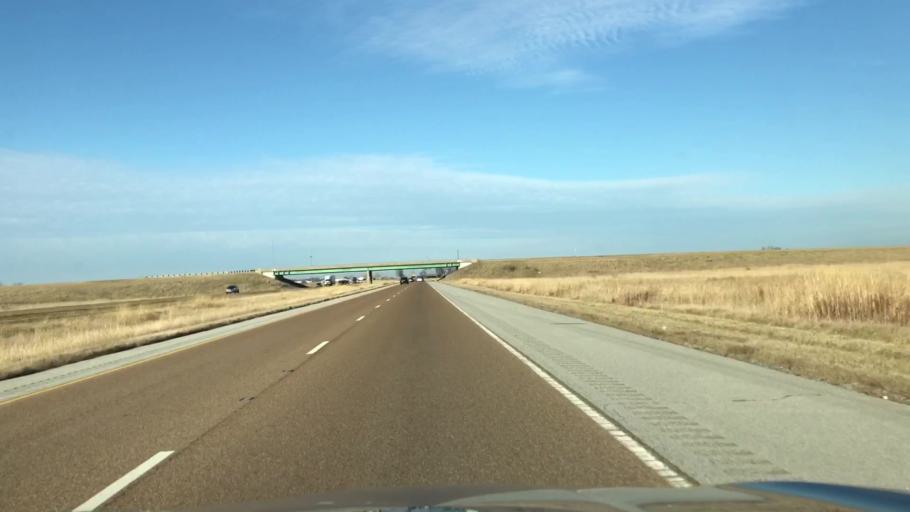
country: US
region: Illinois
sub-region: Macoupin County
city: Staunton
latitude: 39.0182
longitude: -89.7494
